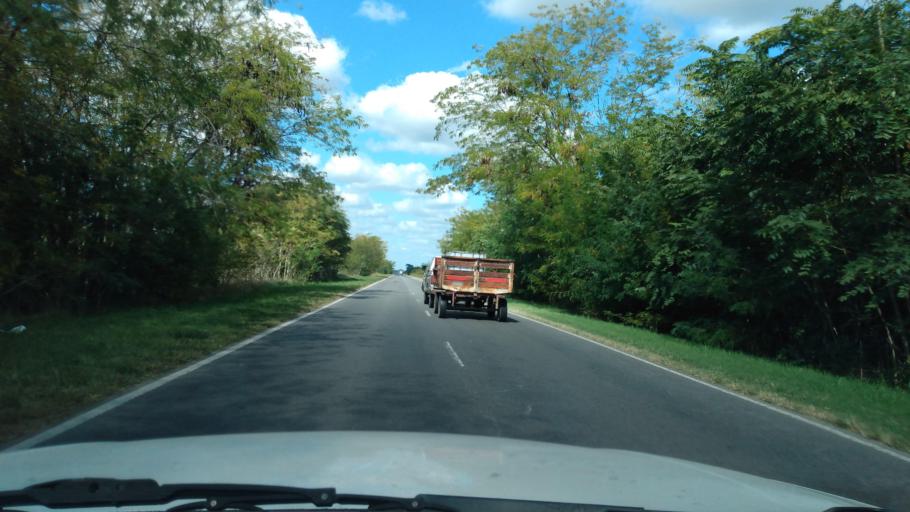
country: AR
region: Buenos Aires
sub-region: Partido de Navarro
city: Navarro
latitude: -34.9433
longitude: -59.3209
